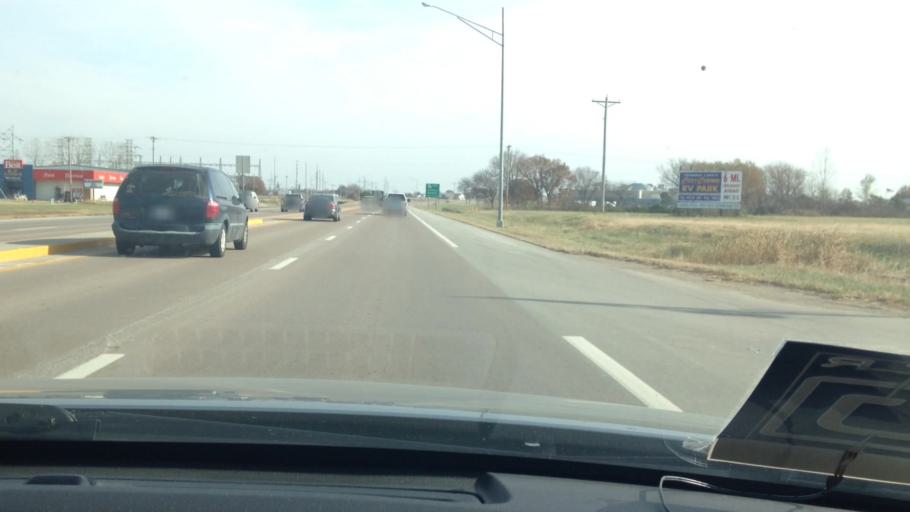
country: US
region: Missouri
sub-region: Henry County
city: Clinton
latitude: 38.3881
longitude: -93.7668
